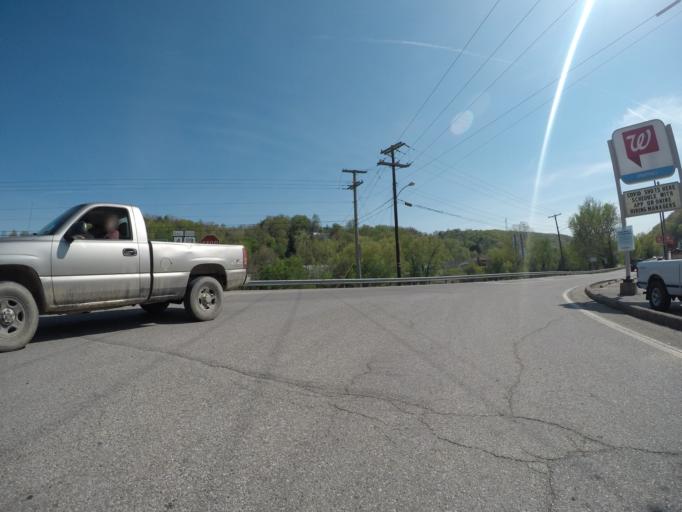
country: US
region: West Virginia
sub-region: Kanawha County
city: Clendenin
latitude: 38.4902
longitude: -81.3501
